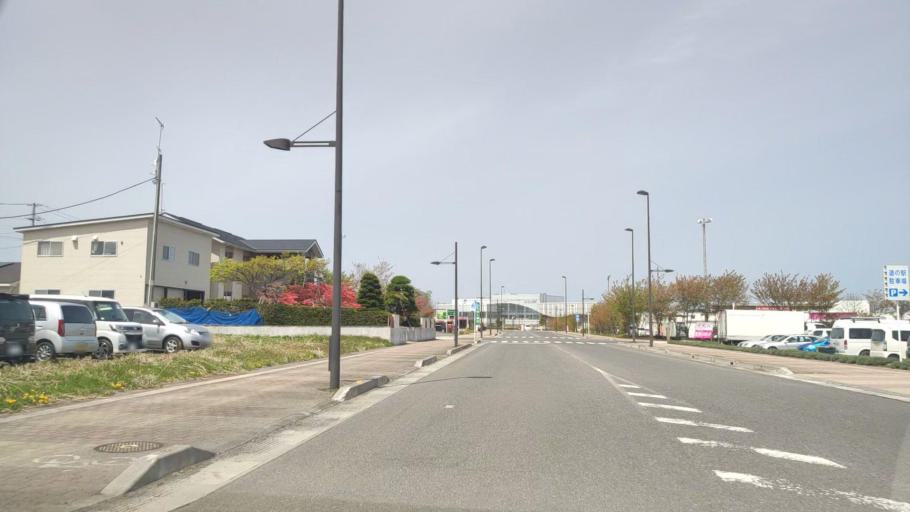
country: JP
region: Aomori
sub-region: Misawa Shi
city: Inuotose
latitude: 40.7169
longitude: 141.1541
